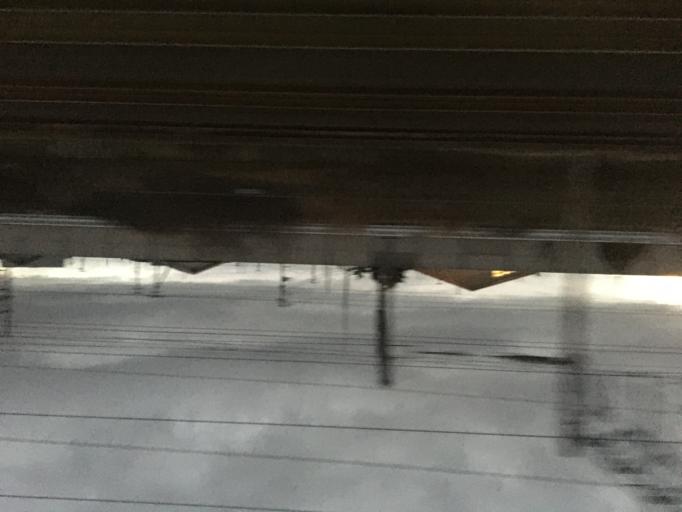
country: JP
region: Aomori
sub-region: Hachinohe Shi
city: Uchimaru
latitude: 40.5137
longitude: 141.4358
